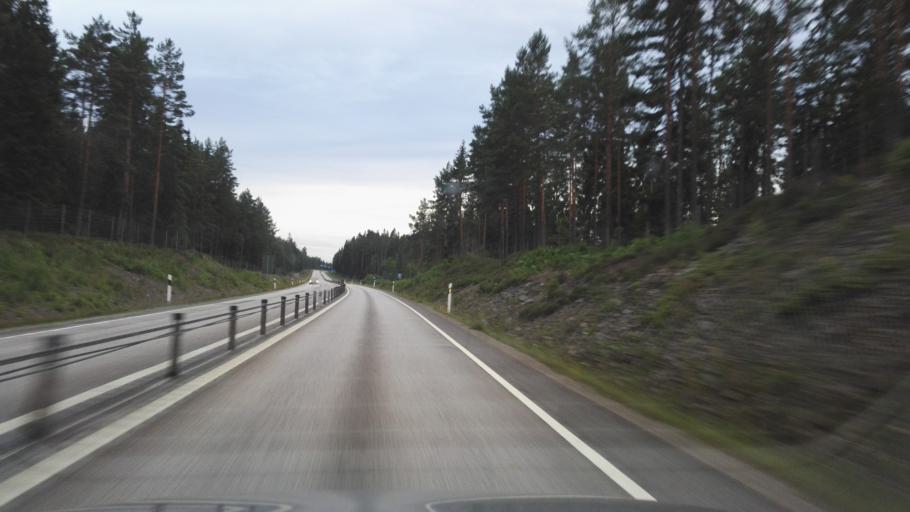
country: SE
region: Kronoberg
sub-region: Vaxjo Kommun
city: Braas
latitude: 57.0268
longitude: 15.0608
